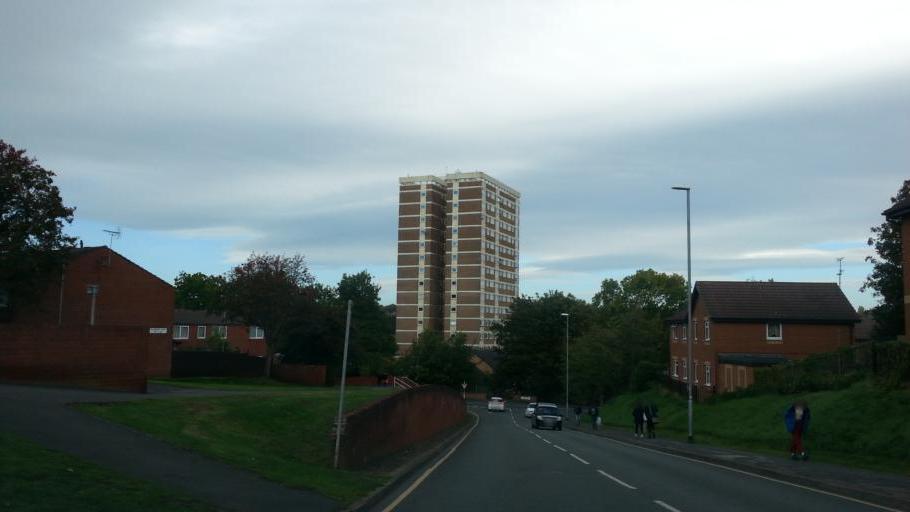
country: GB
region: England
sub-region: City and Borough of Leeds
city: Leeds
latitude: 53.8102
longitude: -1.5506
